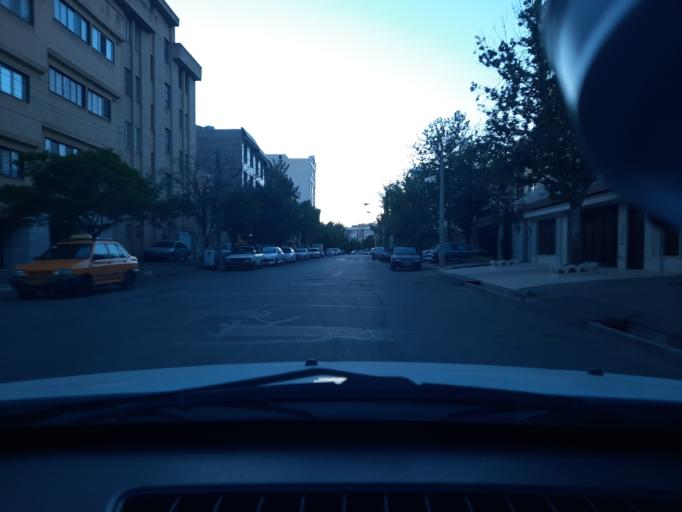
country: IR
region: Qazvin
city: Qazvin
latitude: 36.2980
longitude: 50.0172
